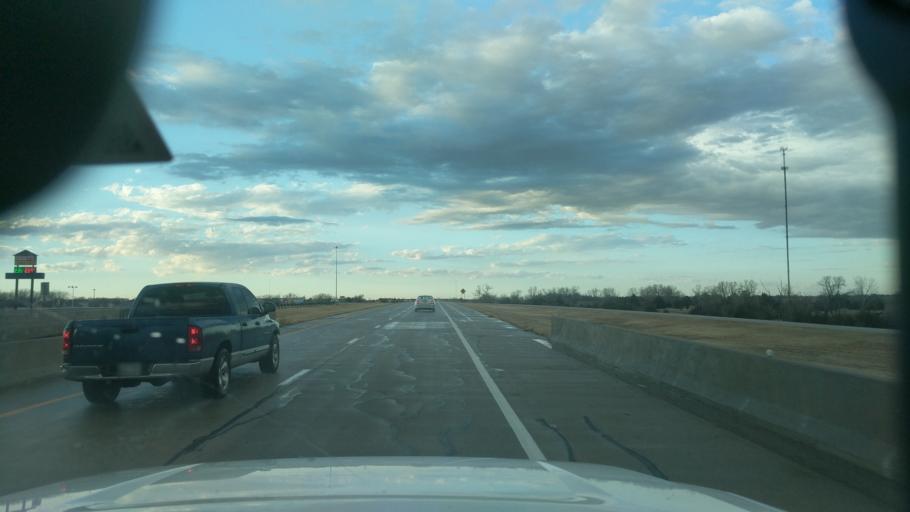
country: US
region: Kansas
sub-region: Harvey County
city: Hesston
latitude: 38.1447
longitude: -97.4171
